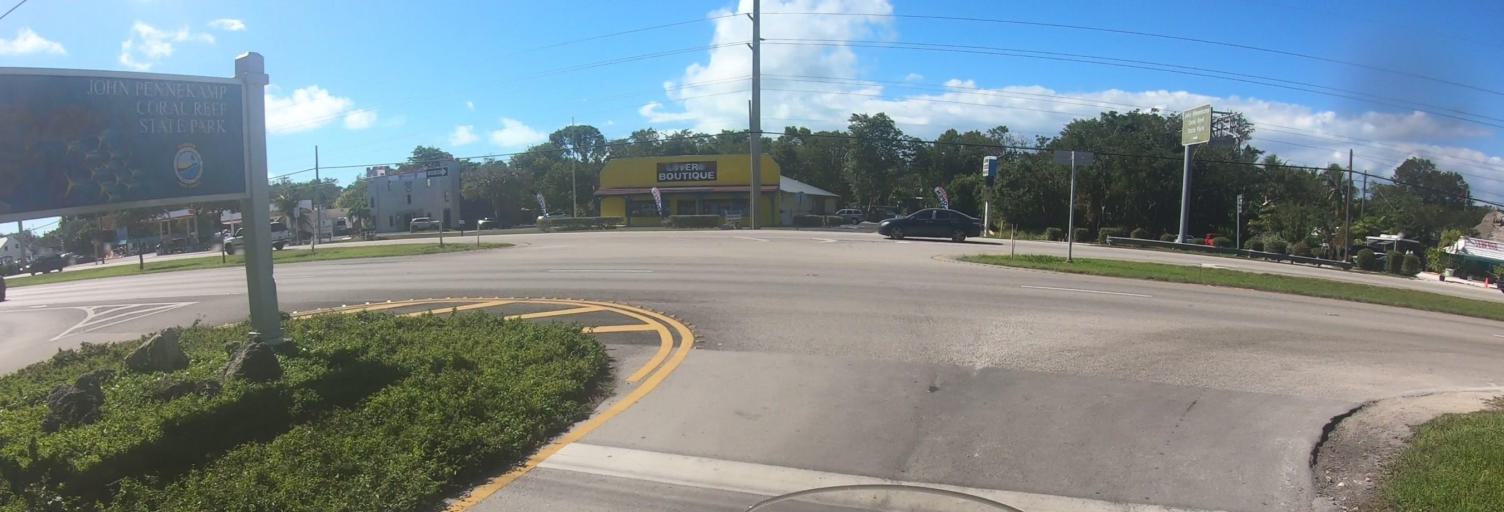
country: US
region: Florida
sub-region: Monroe County
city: Key Largo
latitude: 25.1281
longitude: -80.4101
